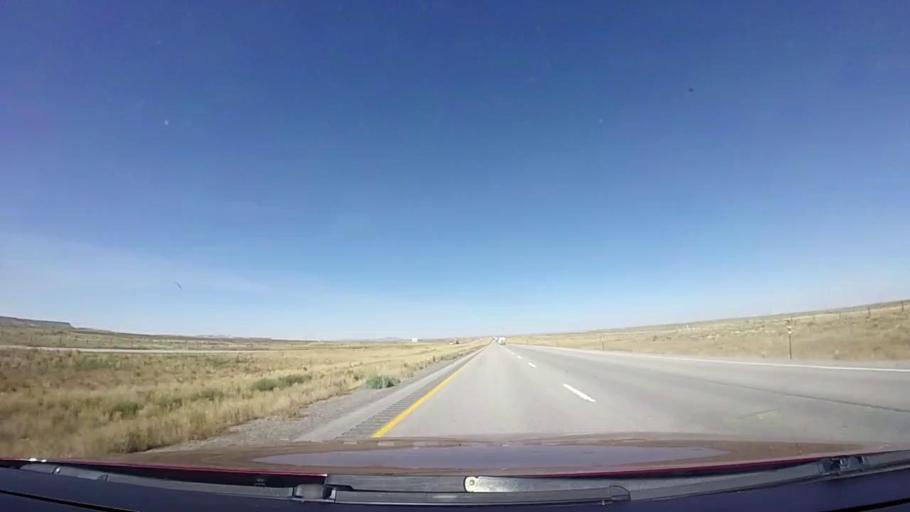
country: US
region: Wyoming
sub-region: Sweetwater County
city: Rock Springs
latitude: 41.6309
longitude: -108.3214
